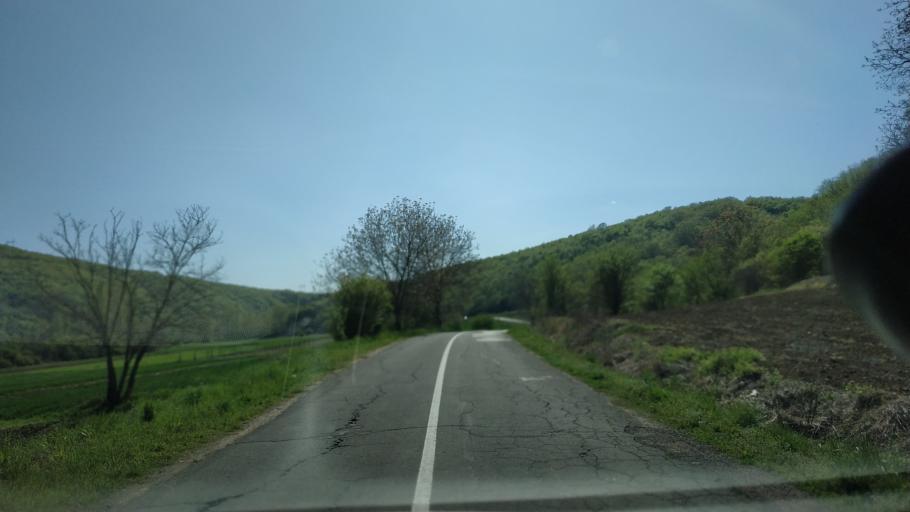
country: RS
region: Central Serbia
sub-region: Nisavski Okrug
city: Nis
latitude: 43.4127
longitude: 21.8294
